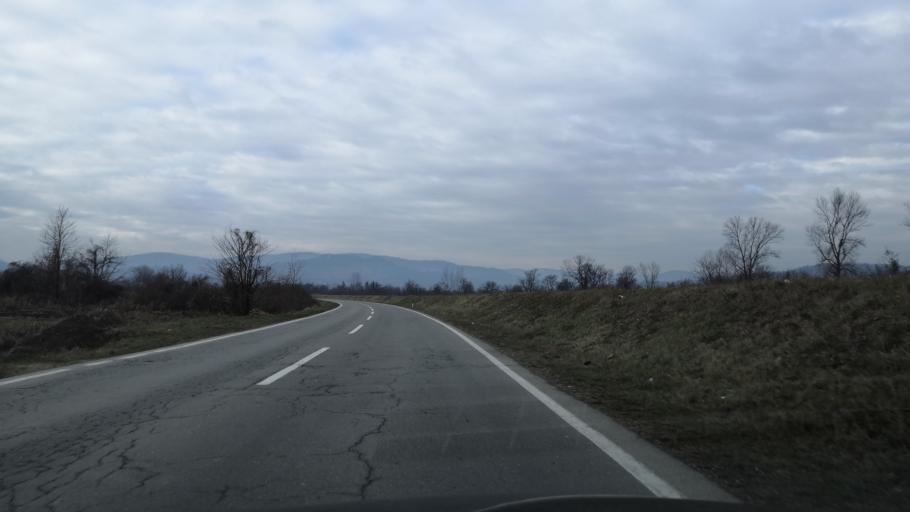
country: BA
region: Republika Srpska
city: Petkovci
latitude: 44.5224
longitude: 19.1414
